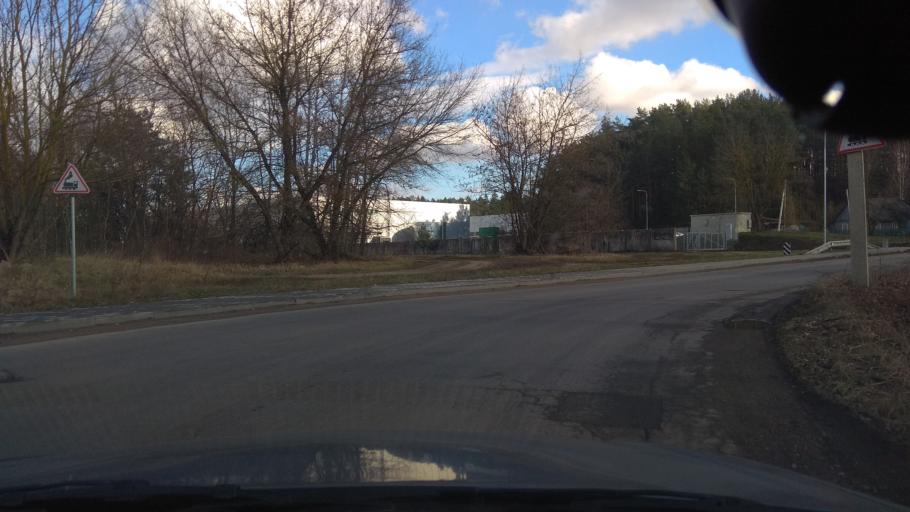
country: LT
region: Vilnius County
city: Lazdynai
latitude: 54.6462
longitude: 25.2184
